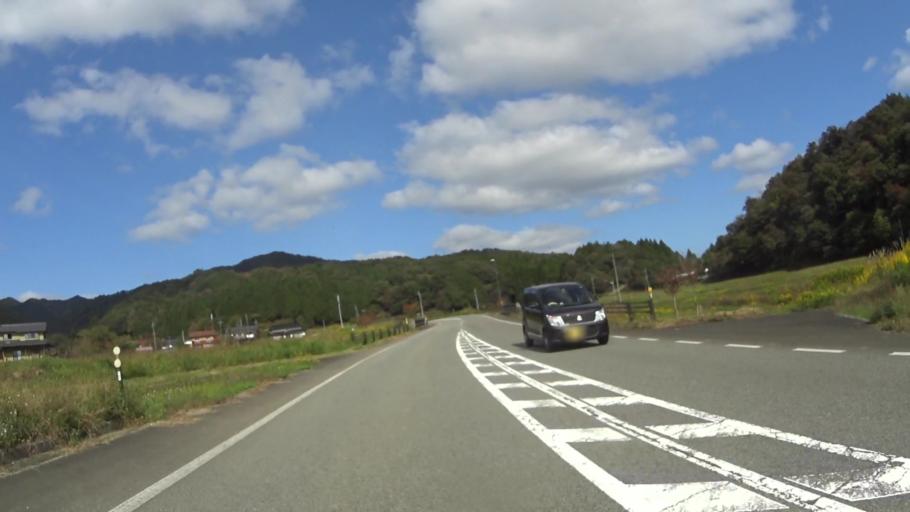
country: JP
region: Hyogo
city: Toyooka
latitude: 35.5071
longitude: 134.9914
